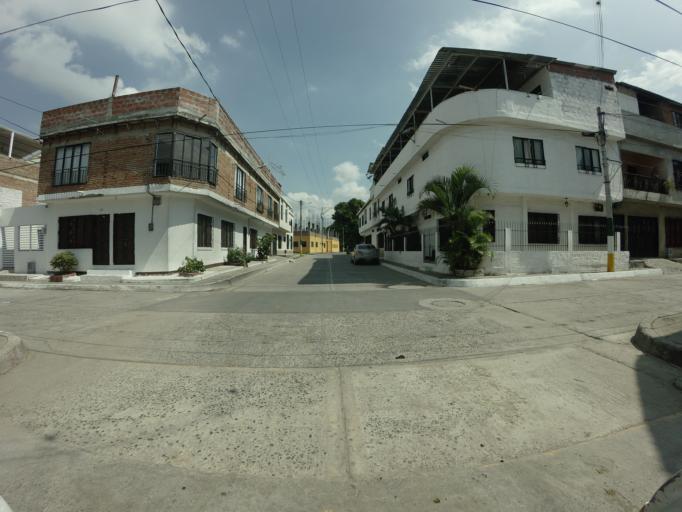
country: CO
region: Valle del Cauca
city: Florida
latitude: 3.3184
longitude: -76.2274
